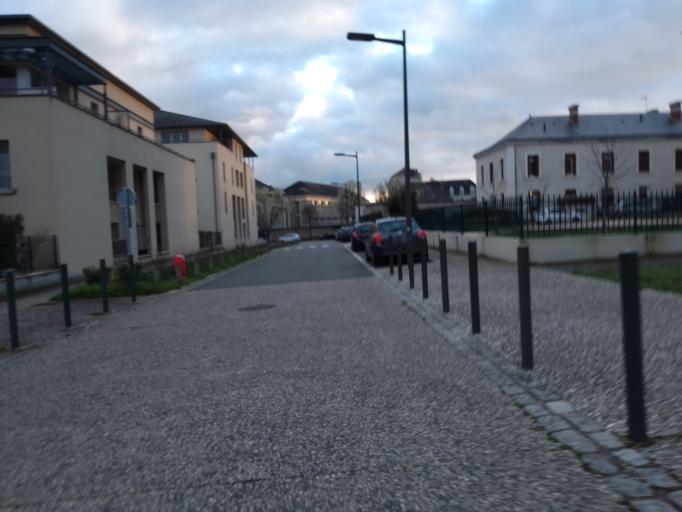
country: FR
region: Centre
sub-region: Departement du Loir-et-Cher
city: Blois
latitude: 47.5935
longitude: 1.3412
